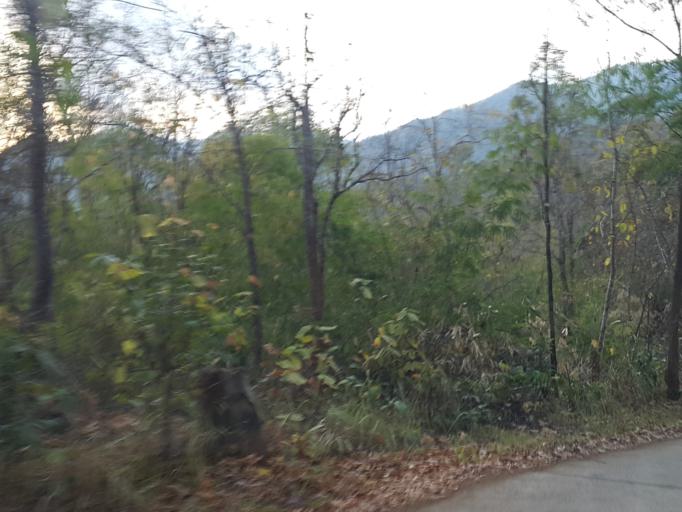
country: TH
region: Lampang
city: Mueang Pan
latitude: 18.8188
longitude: 99.4686
